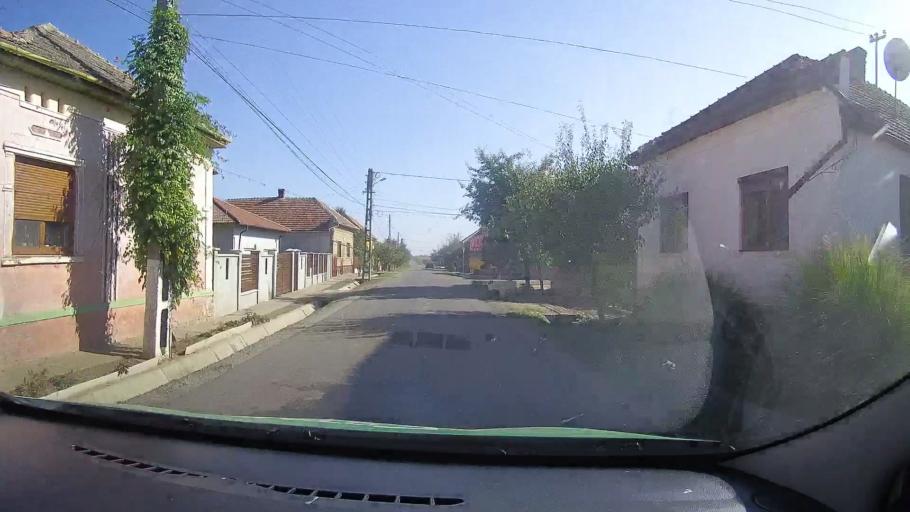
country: RO
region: Satu Mare
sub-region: Comuna Urziceni
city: Urziceni
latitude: 47.7355
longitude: 22.4076
